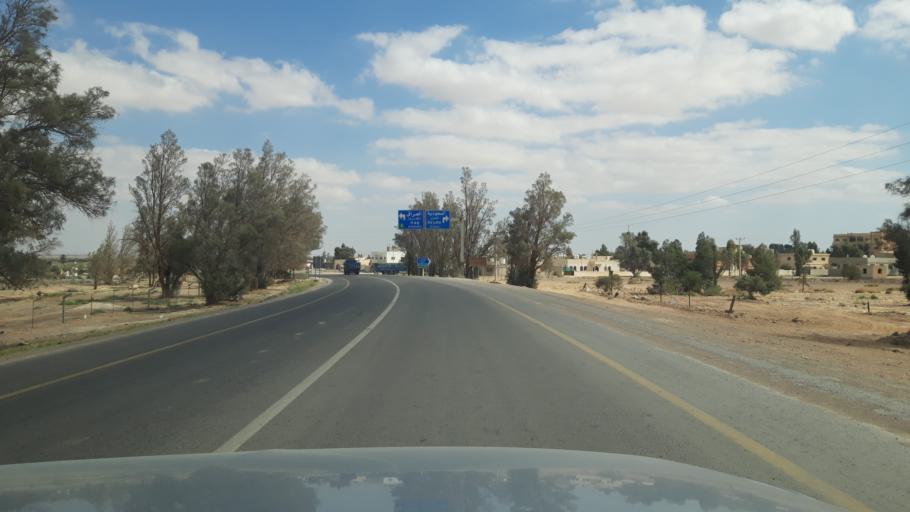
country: JO
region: Amman
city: Al Azraq ash Shamali
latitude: 31.8380
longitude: 36.8113
